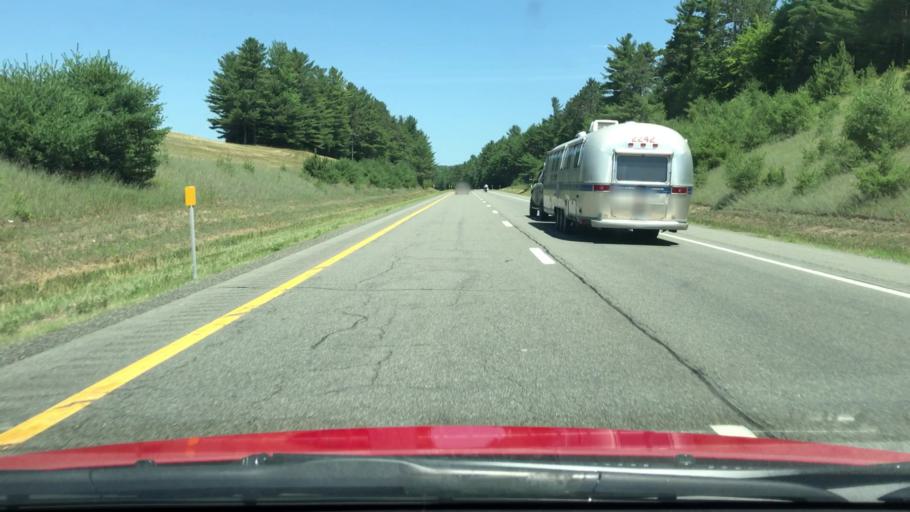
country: US
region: New York
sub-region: Essex County
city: Elizabethtown
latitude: 44.3109
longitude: -73.5290
